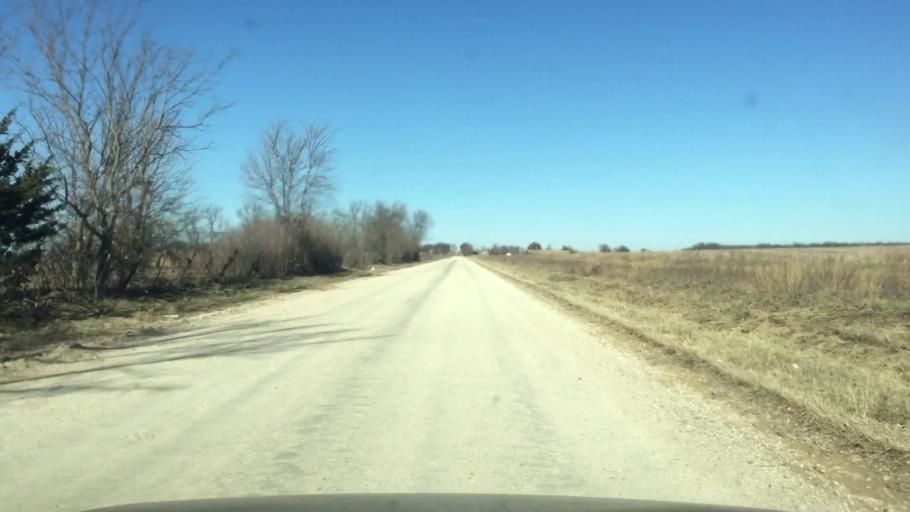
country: US
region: Kansas
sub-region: Allen County
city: Iola
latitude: 37.8697
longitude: -95.3911
